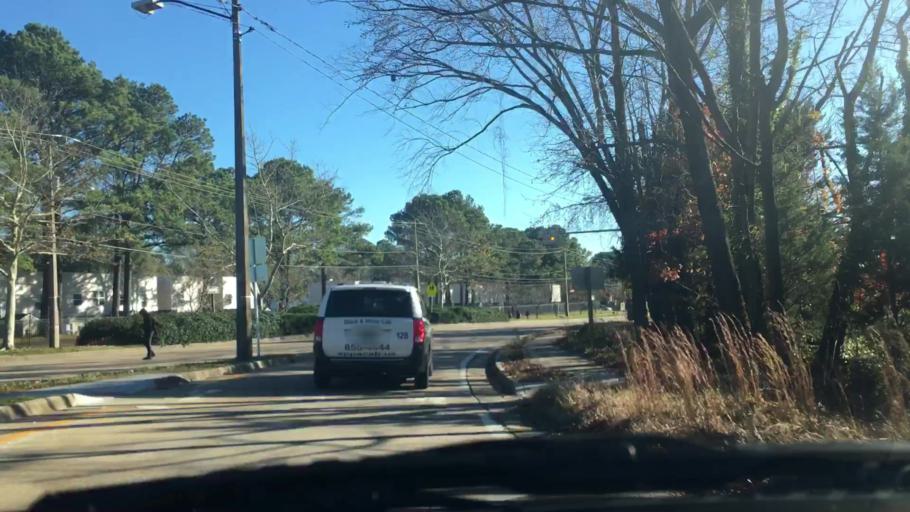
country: US
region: Virginia
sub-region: City of Norfolk
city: Norfolk
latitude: 36.9017
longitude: -76.2397
